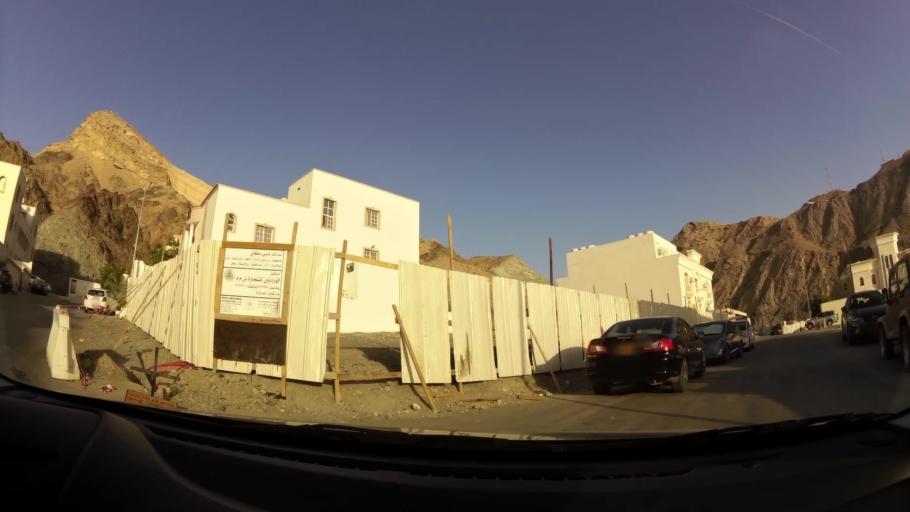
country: OM
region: Muhafazat Masqat
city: Muscat
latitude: 23.5647
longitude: 58.5842
